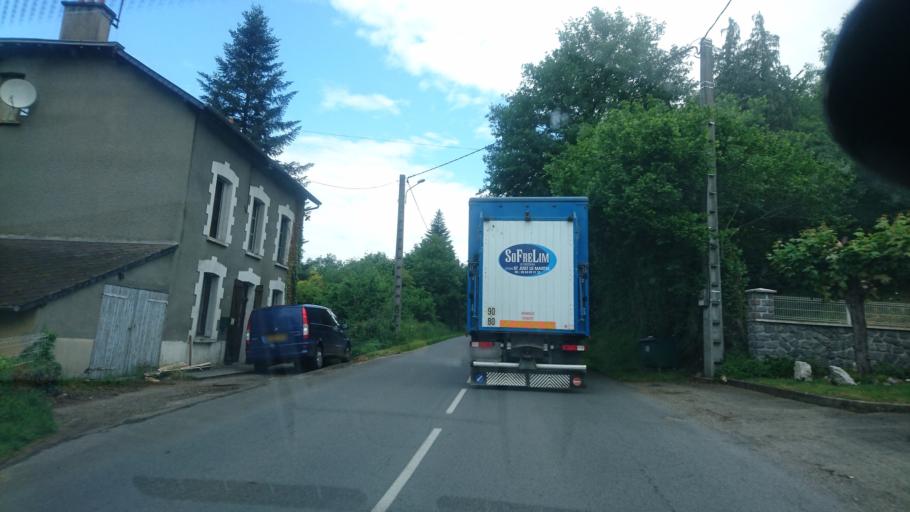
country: FR
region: Limousin
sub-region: Departement de la Haute-Vienne
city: Neuvic-Entier
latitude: 45.7206
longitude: 1.6075
